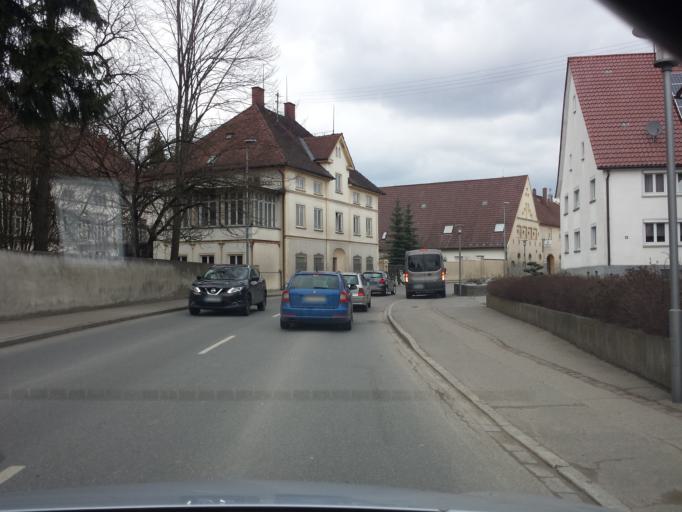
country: DE
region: Baden-Wuerttemberg
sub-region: Tuebingen Region
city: Schwendi
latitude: 48.1766
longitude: 9.9754
